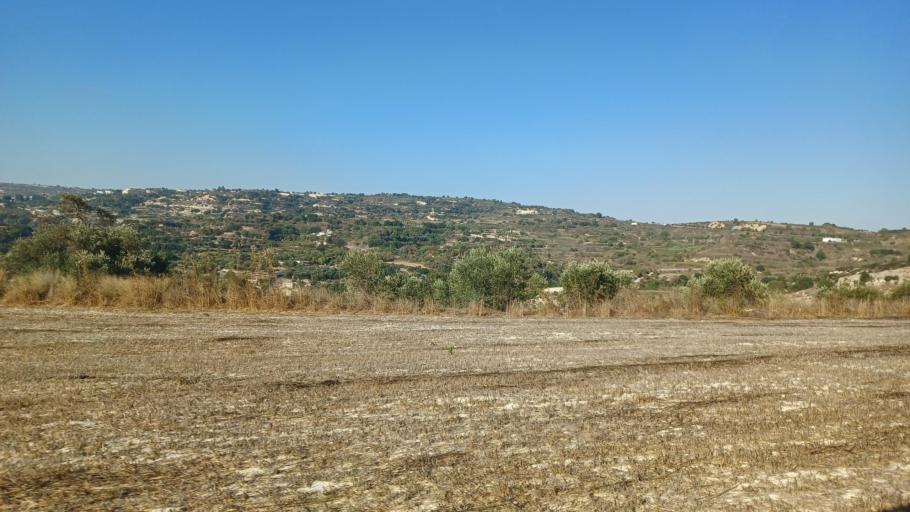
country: CY
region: Pafos
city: Mesogi
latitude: 34.8607
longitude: 32.5140
